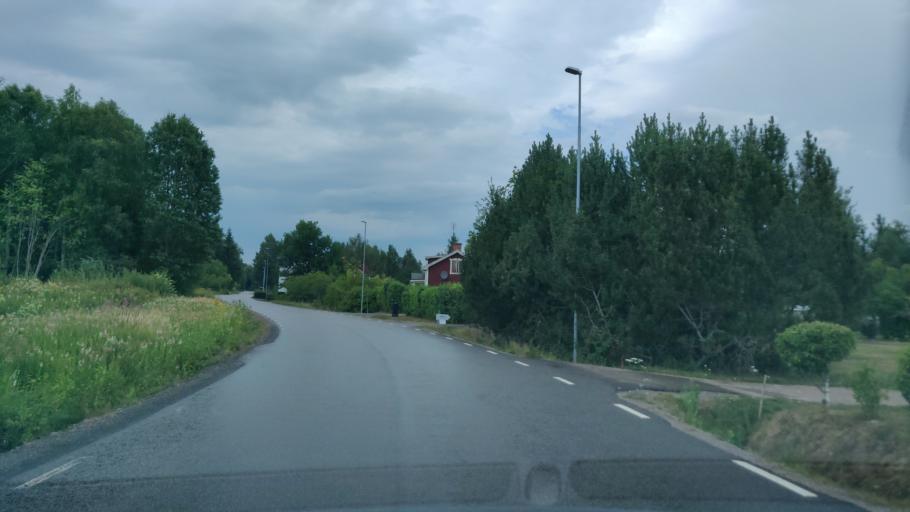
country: SE
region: Vaermland
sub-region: Munkfors Kommun
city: Munkfors
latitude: 59.8545
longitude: 13.5541
